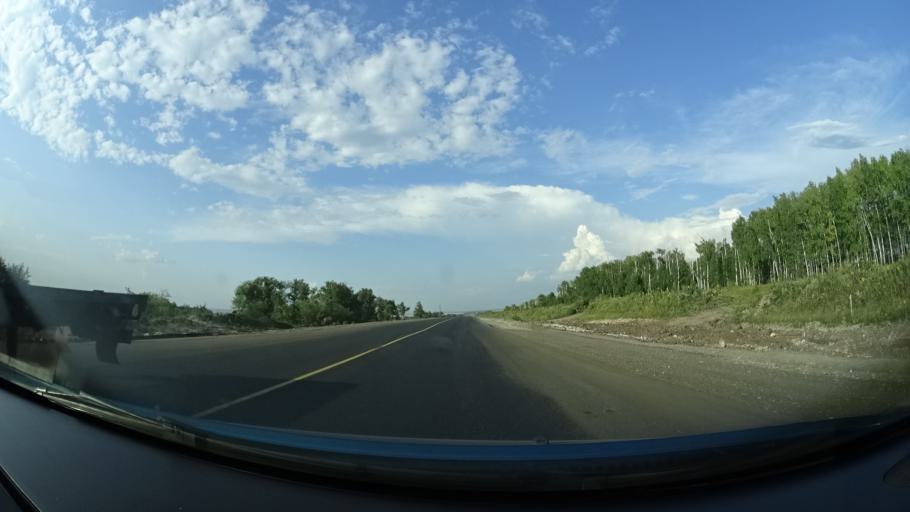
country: RU
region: Samara
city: Sukhodol
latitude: 53.7422
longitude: 50.8564
